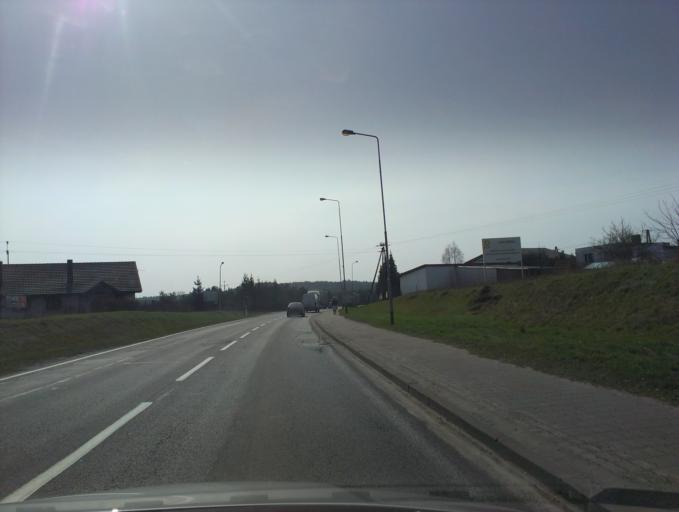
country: PL
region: Greater Poland Voivodeship
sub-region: Powiat zlotowski
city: Okonek
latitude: 53.5332
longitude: 16.8541
